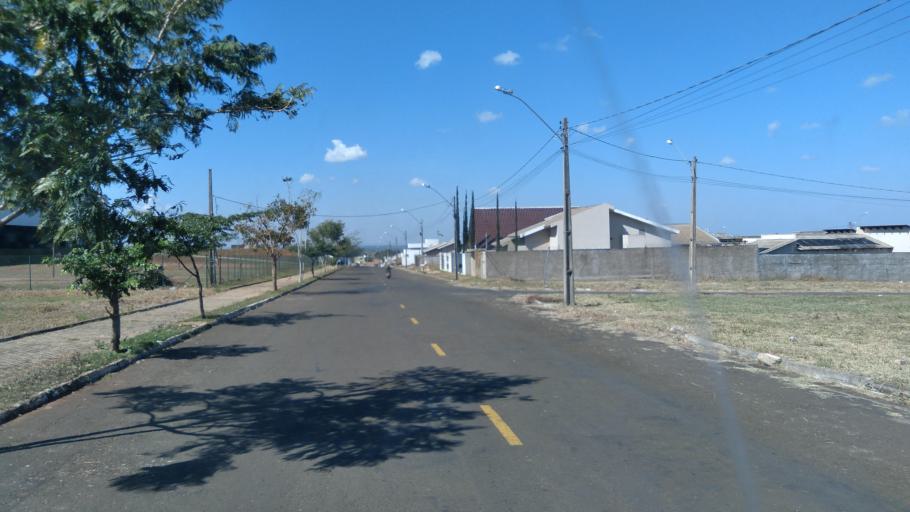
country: BR
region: Goias
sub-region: Mineiros
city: Mineiros
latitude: -17.5499
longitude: -52.5455
